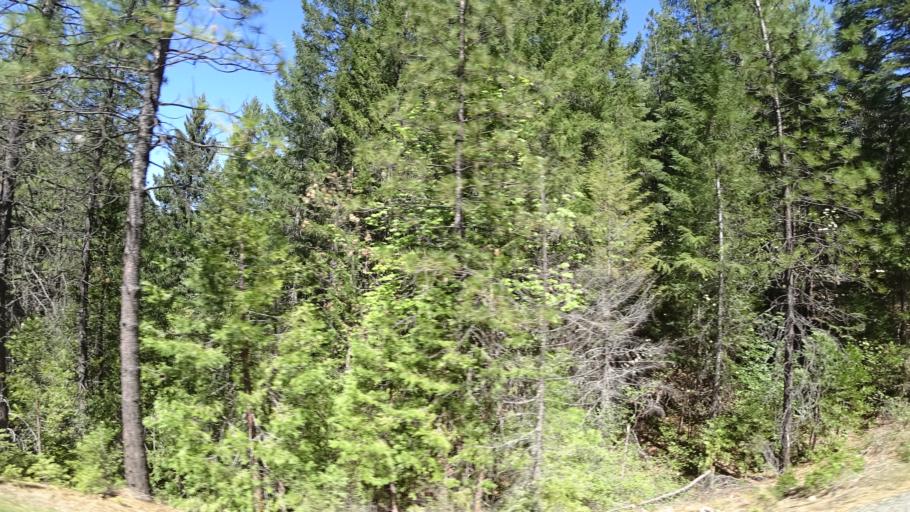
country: US
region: California
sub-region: Trinity County
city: Lewiston
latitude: 40.9013
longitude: -122.7867
